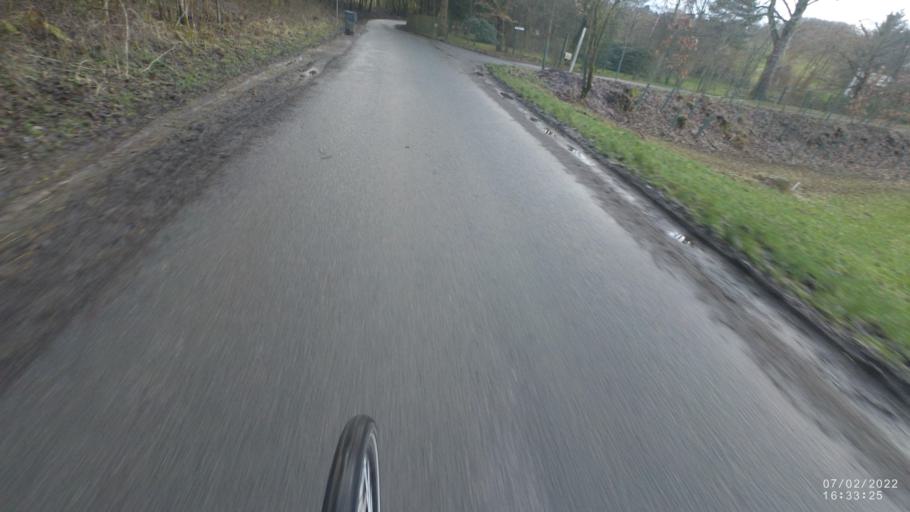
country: DE
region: North Rhine-Westphalia
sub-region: Regierungsbezirk Arnsberg
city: Luedenscheid
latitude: 51.2557
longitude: 7.5985
